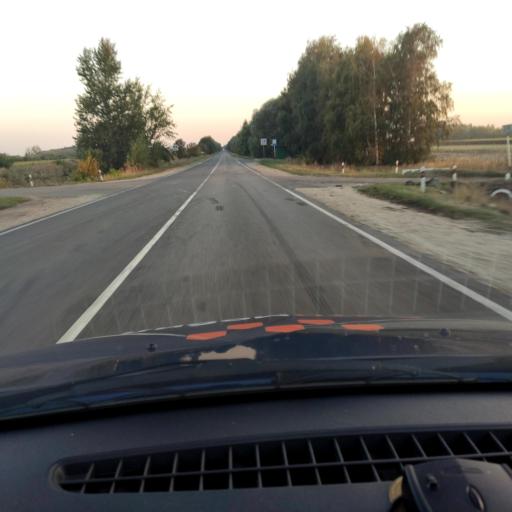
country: RU
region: Voronezj
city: Latnaya
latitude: 51.6245
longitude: 38.7798
